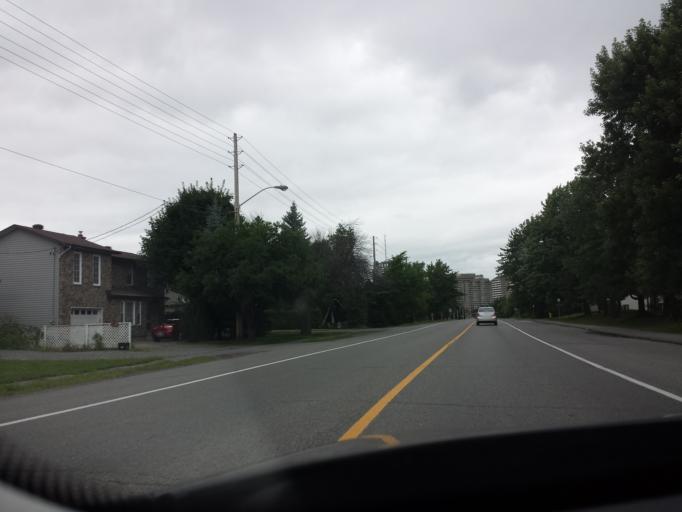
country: CA
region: Ontario
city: Ottawa
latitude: 45.3623
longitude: -75.7002
